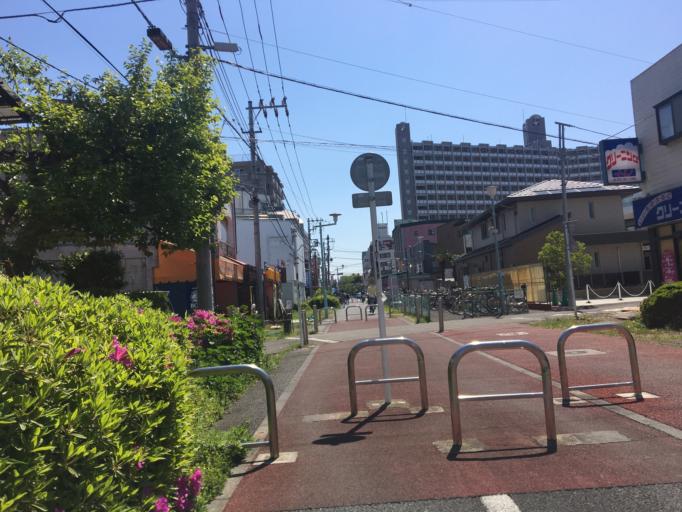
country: JP
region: Tokyo
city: Higashimurayama-shi
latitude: 35.7372
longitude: 139.4862
